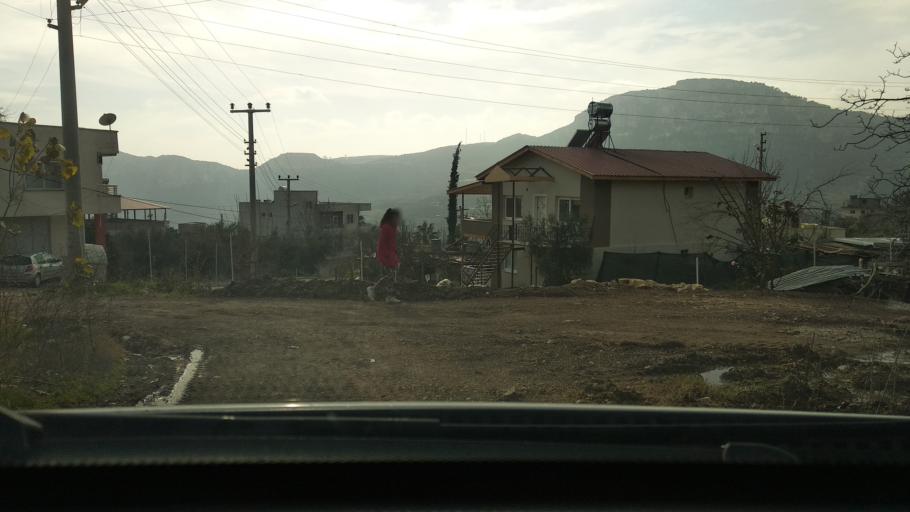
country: TR
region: Mersin
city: Kuzucubelen
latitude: 36.8764
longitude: 34.4665
